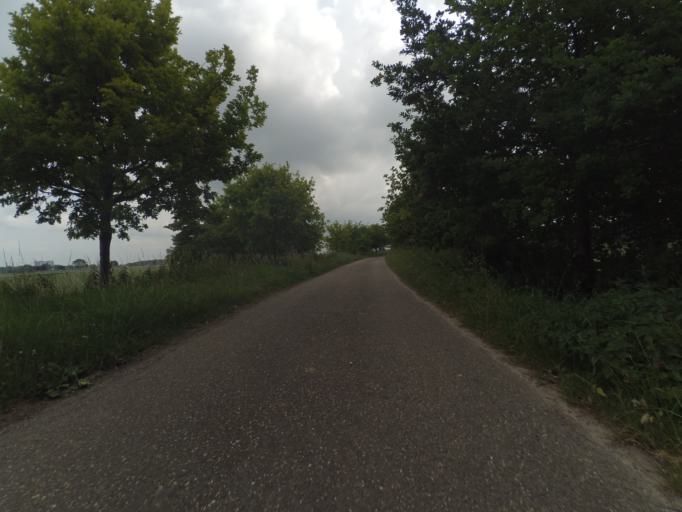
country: NL
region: North Brabant
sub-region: Gemeente Moerdijk
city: Klundert
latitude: 51.6310
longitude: 4.6081
